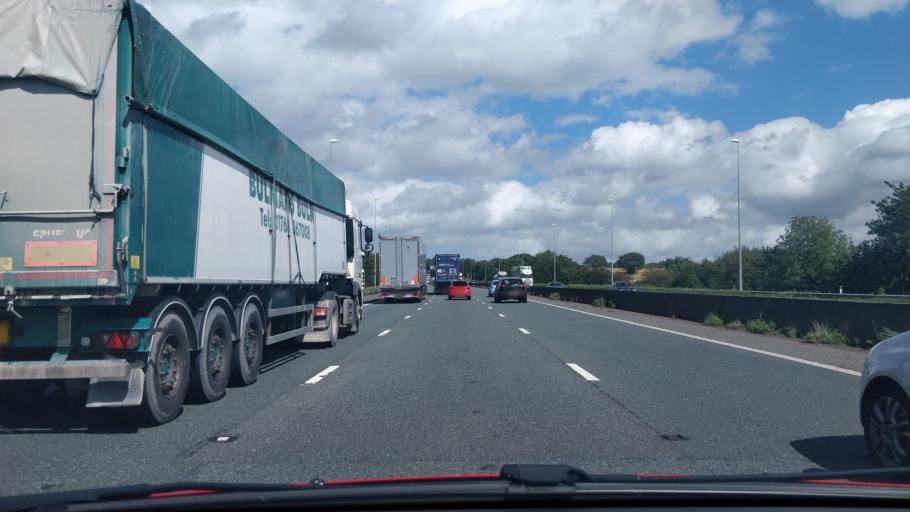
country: GB
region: England
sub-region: Borough of Wigan
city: Shevington
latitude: 53.5760
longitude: -2.6963
